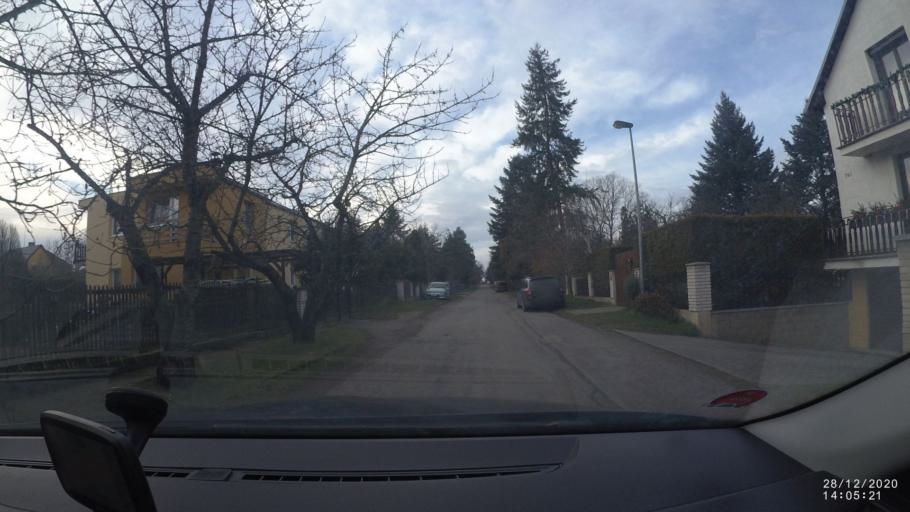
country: CZ
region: Central Bohemia
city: Sestajovice
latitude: 50.0995
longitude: 14.6688
